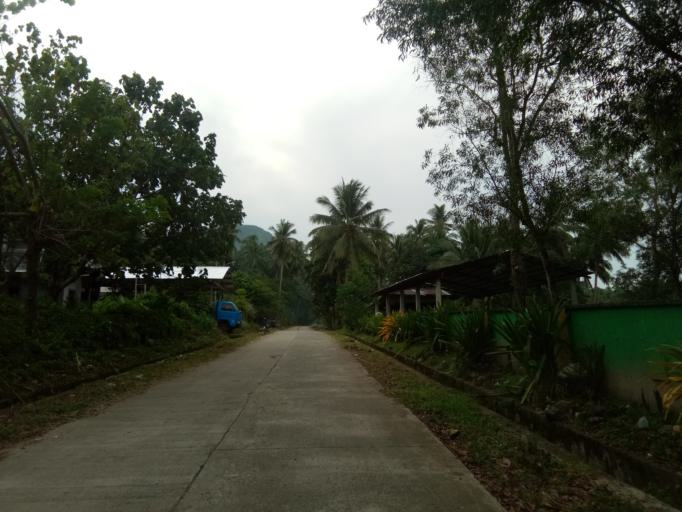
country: PH
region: Caraga
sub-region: Province of Surigao del Norte
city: Tubod
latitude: 9.5661
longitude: 125.5678
